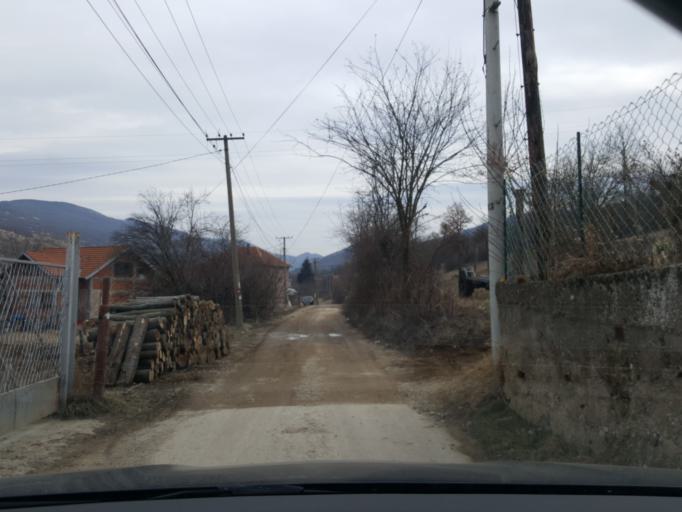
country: RS
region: Central Serbia
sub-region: Pirotski Okrug
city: Dimitrovgrad
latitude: 43.0080
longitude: 22.7539
